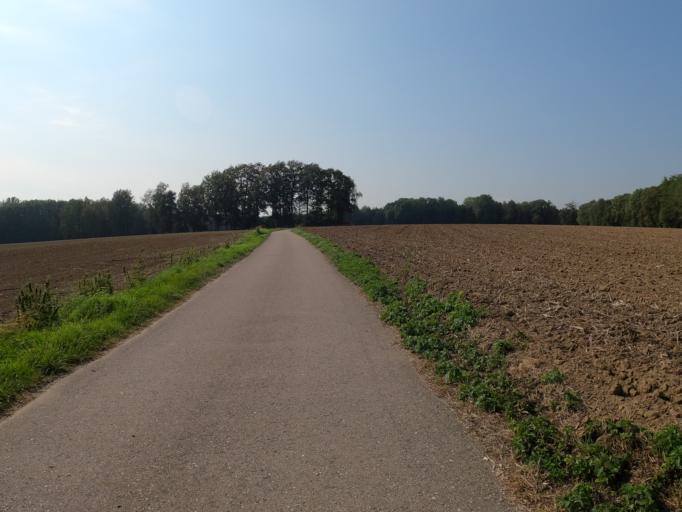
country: DE
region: Bavaria
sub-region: Swabia
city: Rettenbach
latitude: 48.4702
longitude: 10.3312
